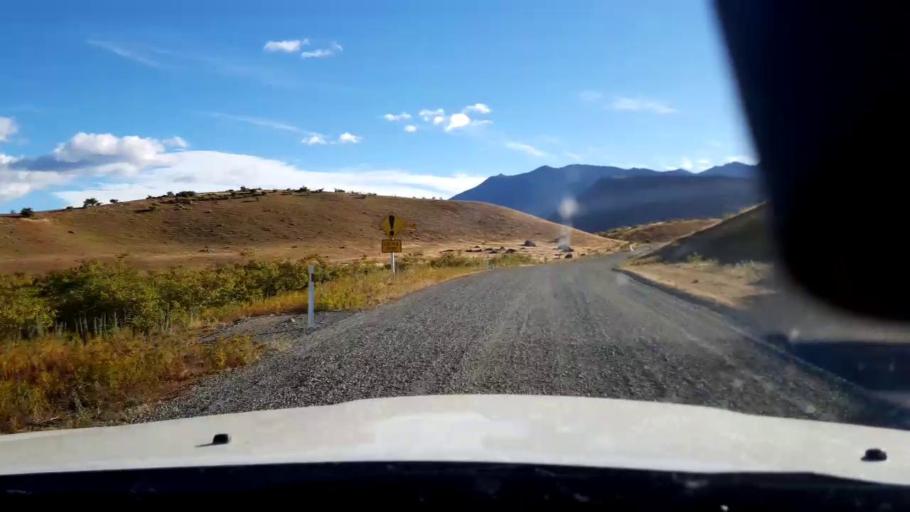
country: NZ
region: Canterbury
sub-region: Timaru District
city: Pleasant Point
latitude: -43.9663
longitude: 170.5189
